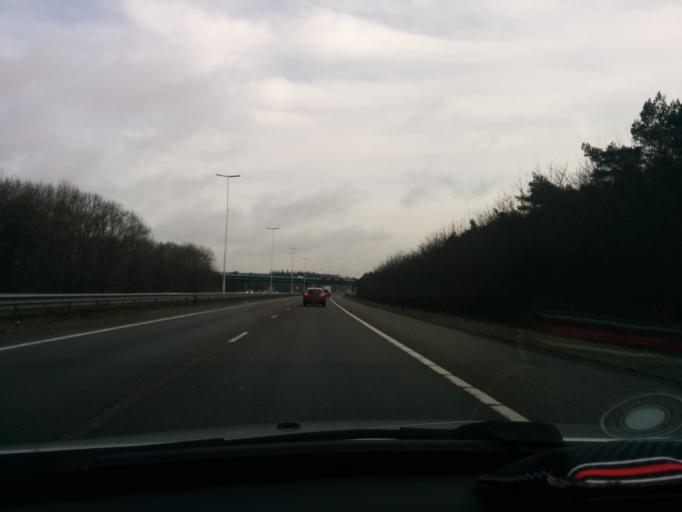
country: NL
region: North Holland
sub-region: Gemeente Hilversum
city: Hilversum
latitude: 52.2006
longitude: 5.1923
